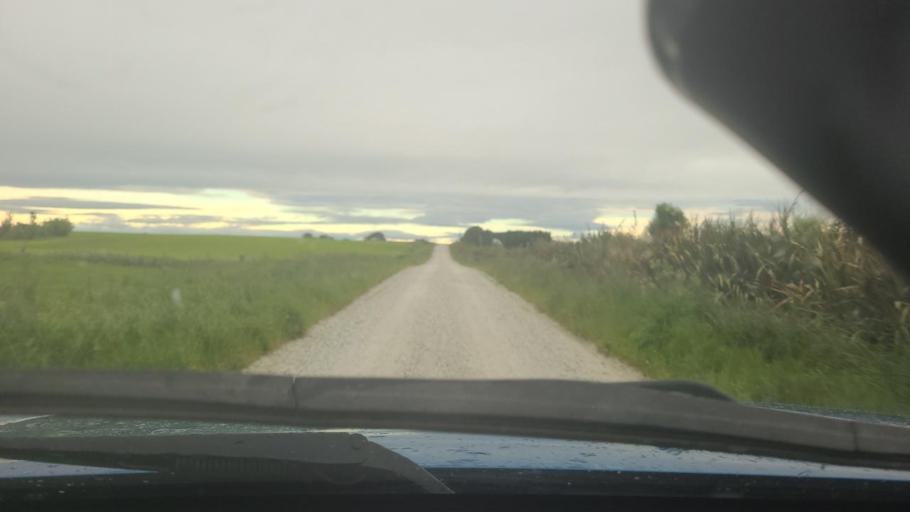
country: NZ
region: Southland
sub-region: Invercargill City
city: Invercargill
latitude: -46.4366
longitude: 168.5396
